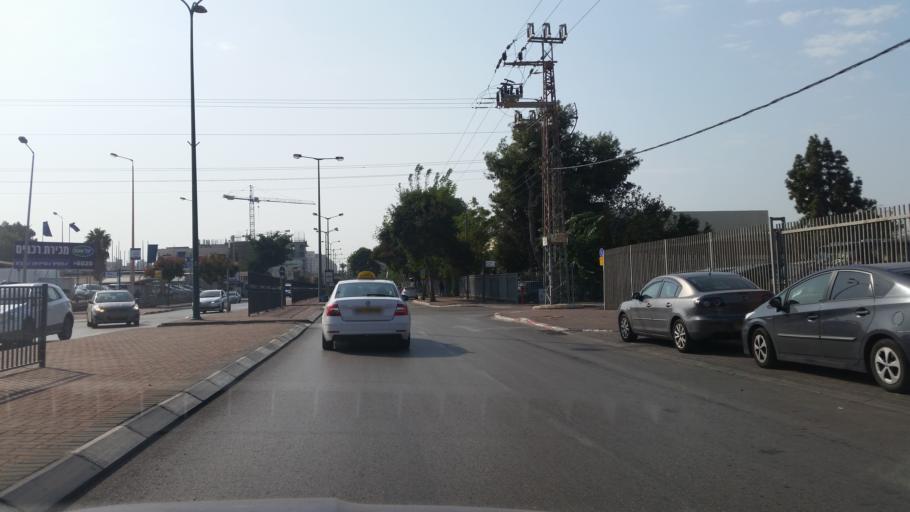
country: IL
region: Central District
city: Bet Yizhaq
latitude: 32.3174
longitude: 34.8739
